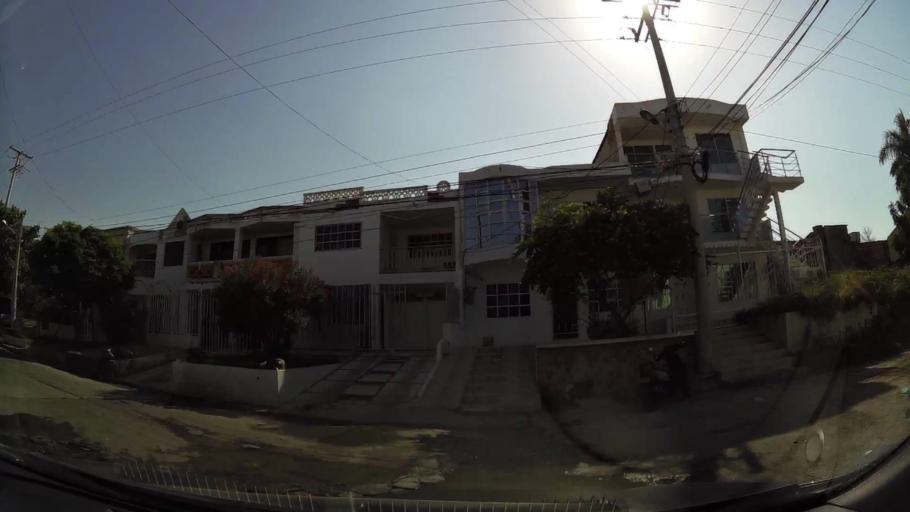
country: CO
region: Bolivar
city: Cartagena
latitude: 10.3816
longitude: -75.4761
